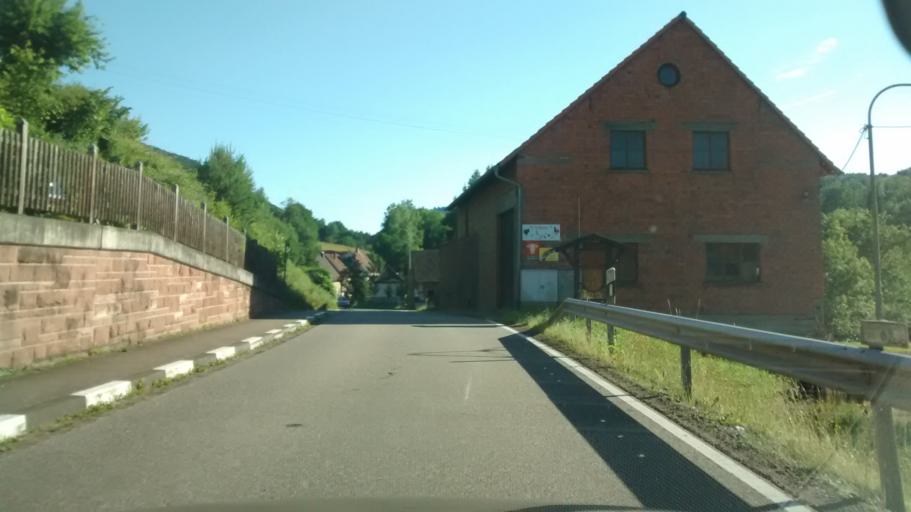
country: DE
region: Rheinland-Pfalz
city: Vorderweidenthal
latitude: 49.1140
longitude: 7.8638
